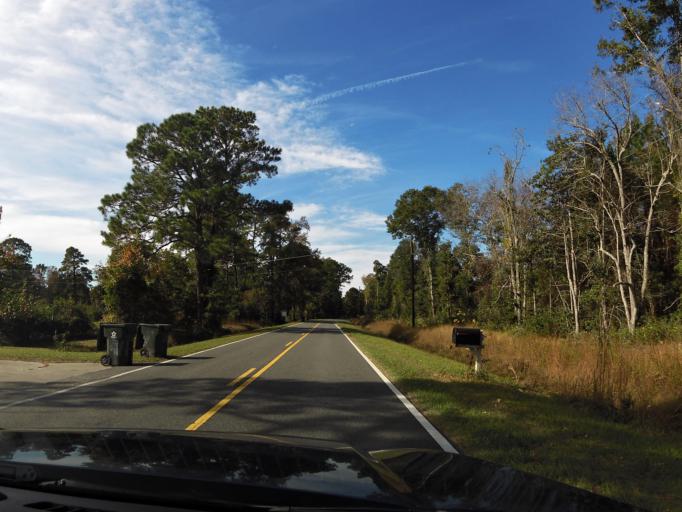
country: US
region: Georgia
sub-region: Glynn County
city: Brunswick
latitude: 31.1399
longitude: -81.5631
